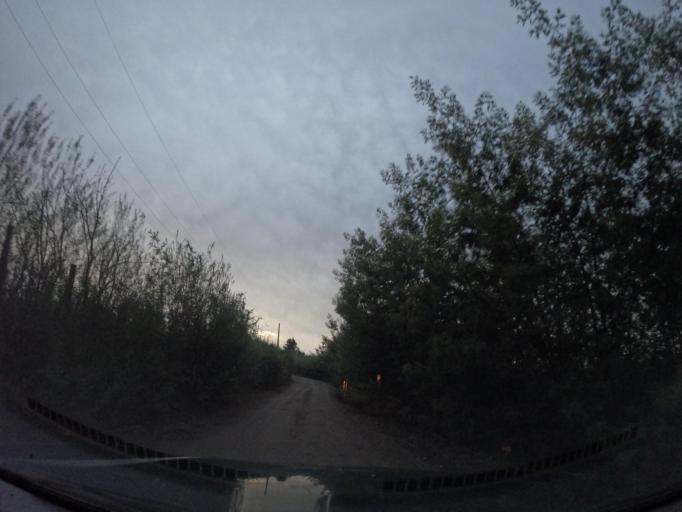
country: CL
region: Biobio
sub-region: Provincia de Concepcion
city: Chiguayante
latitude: -37.0105
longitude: -72.8723
